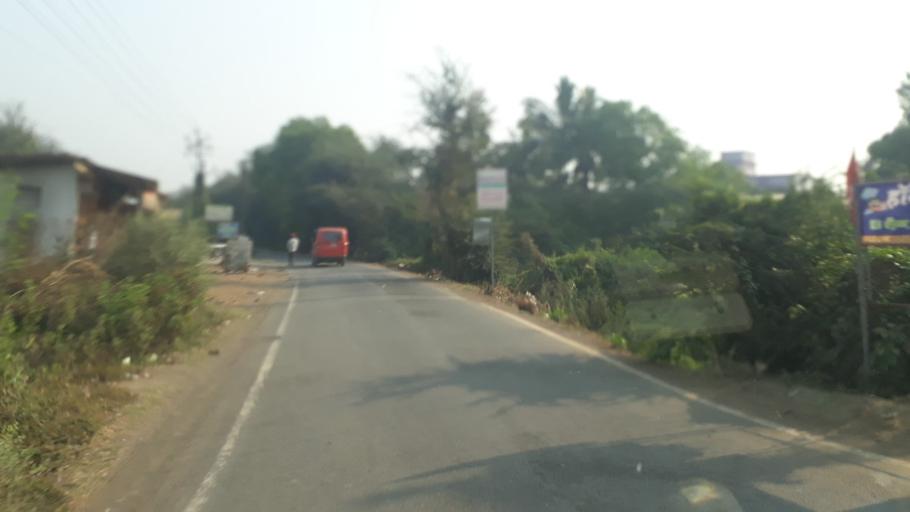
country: IN
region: Maharashtra
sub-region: Raigarh
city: Neral
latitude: 19.0226
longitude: 73.3206
